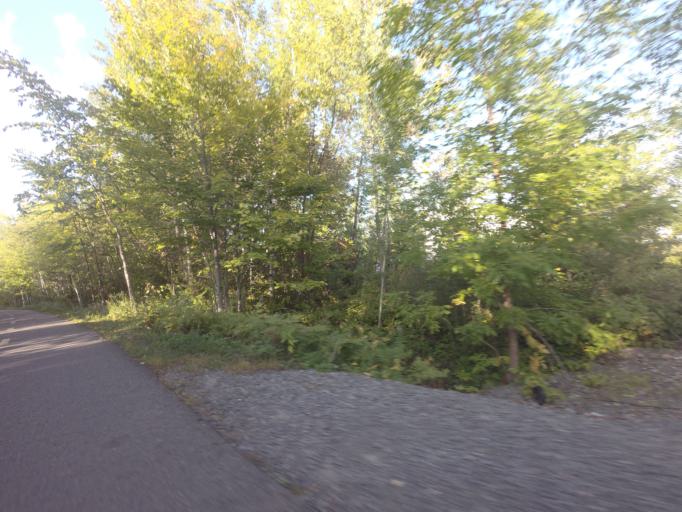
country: CA
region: Quebec
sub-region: Laurentides
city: Saint-Jerome
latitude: 45.7914
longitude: -73.9969
